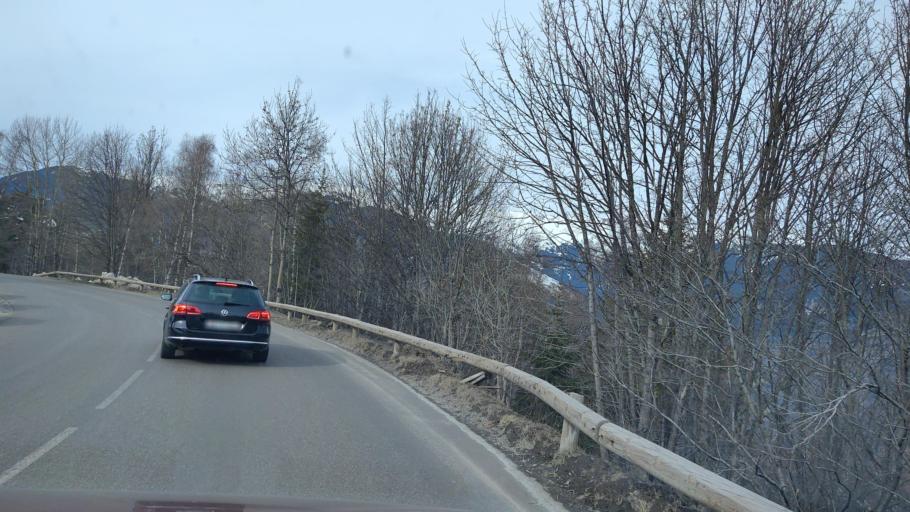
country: FR
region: Rhone-Alpes
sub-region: Departement de la Savoie
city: Saint-Bon-Tarentaise
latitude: 45.4246
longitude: 6.6431
